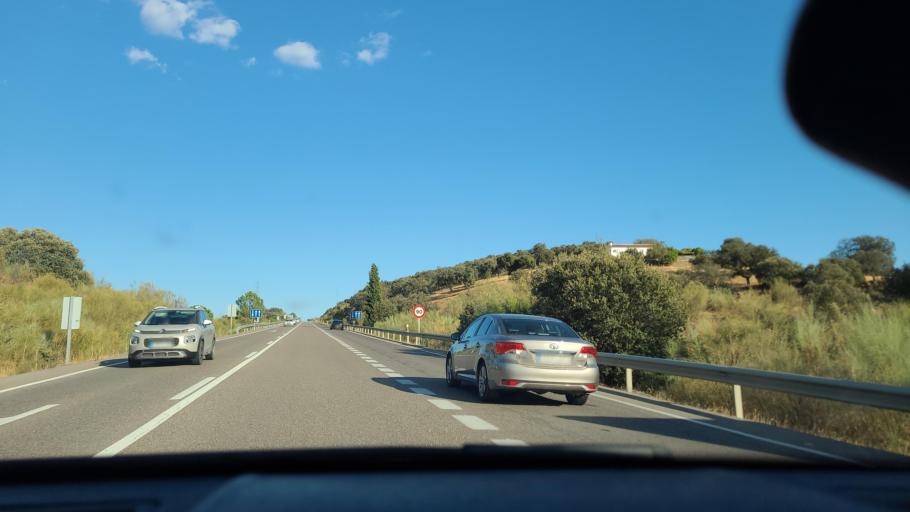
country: ES
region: Andalusia
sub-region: Province of Cordoba
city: Espiel
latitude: 38.1820
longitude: -5.0273
